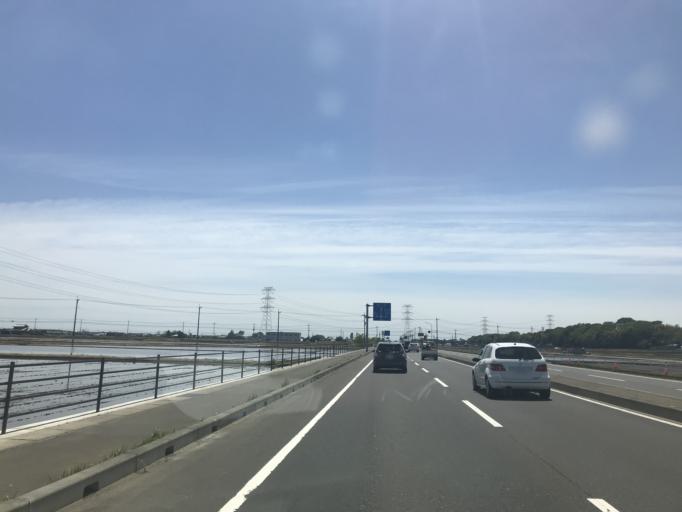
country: JP
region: Ibaraki
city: Shimodate
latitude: 36.2528
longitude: 139.9829
